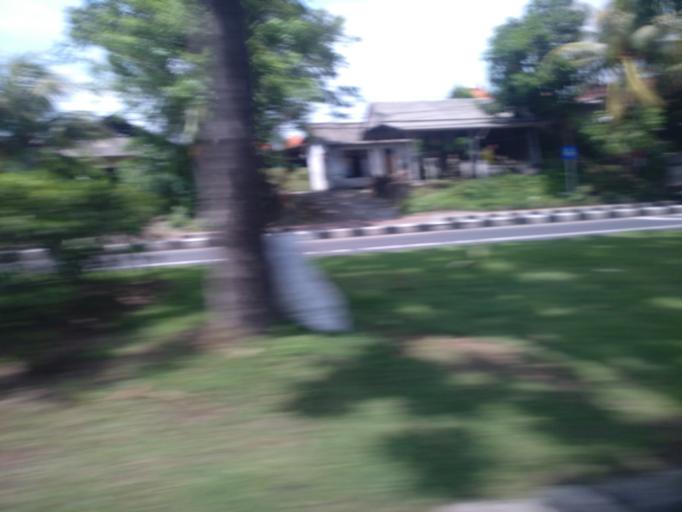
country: ID
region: Bali
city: Banjar Kertajiwa
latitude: -8.6490
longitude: 115.2649
